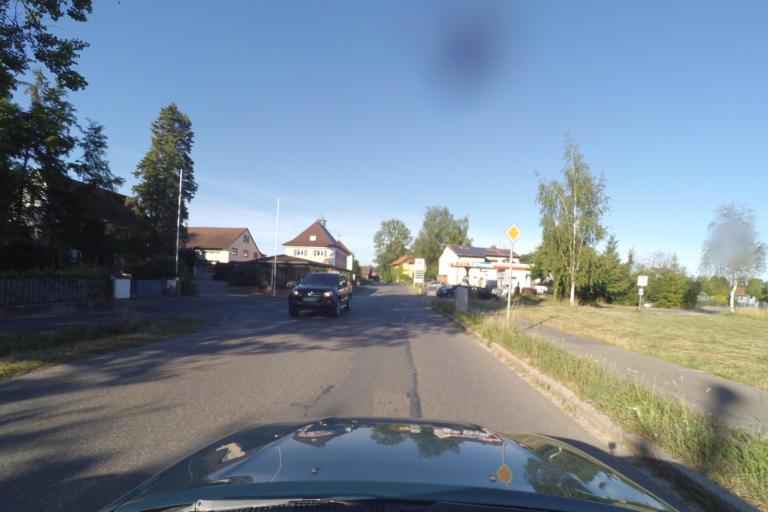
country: DE
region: Bavaria
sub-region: Upper Franconia
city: Speichersdorf
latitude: 49.8756
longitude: 11.7810
